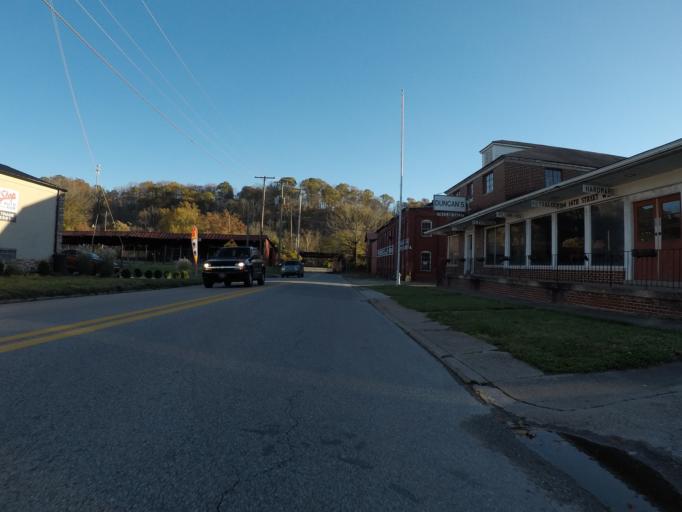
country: US
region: West Virginia
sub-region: Cabell County
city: Huntington
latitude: 38.4065
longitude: -82.4775
